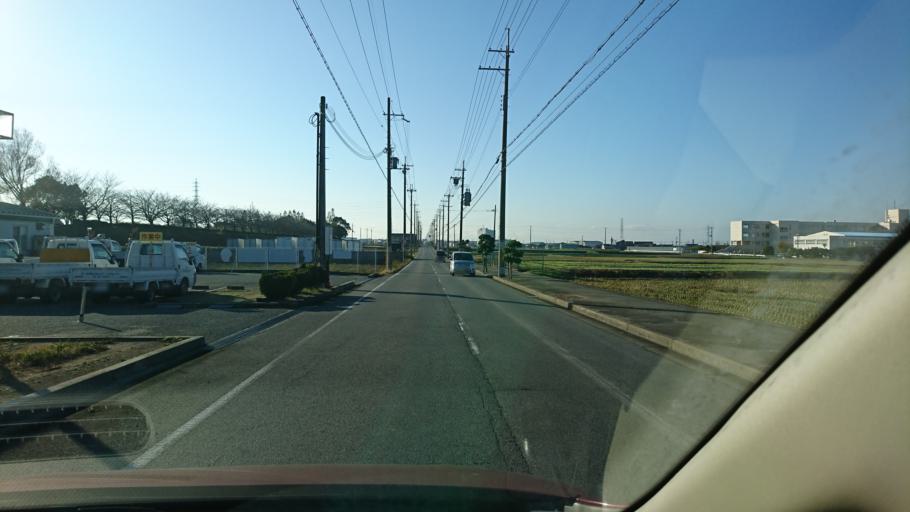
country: JP
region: Hyogo
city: Miki
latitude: 34.7416
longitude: 134.9217
